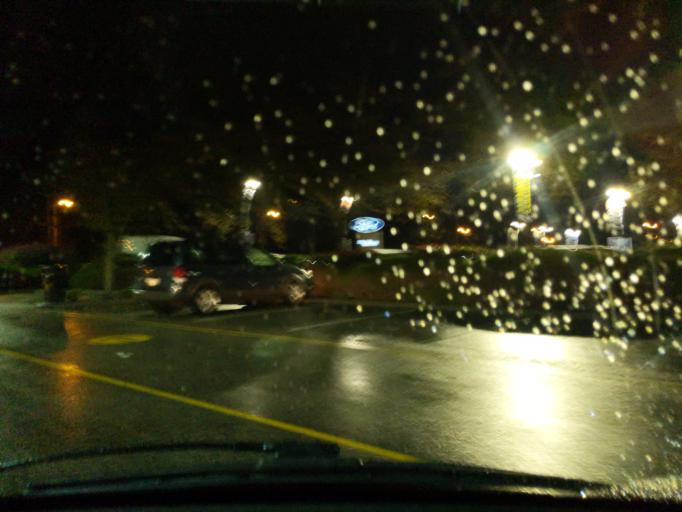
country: CA
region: British Columbia
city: Surrey
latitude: 49.1910
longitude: -122.8206
